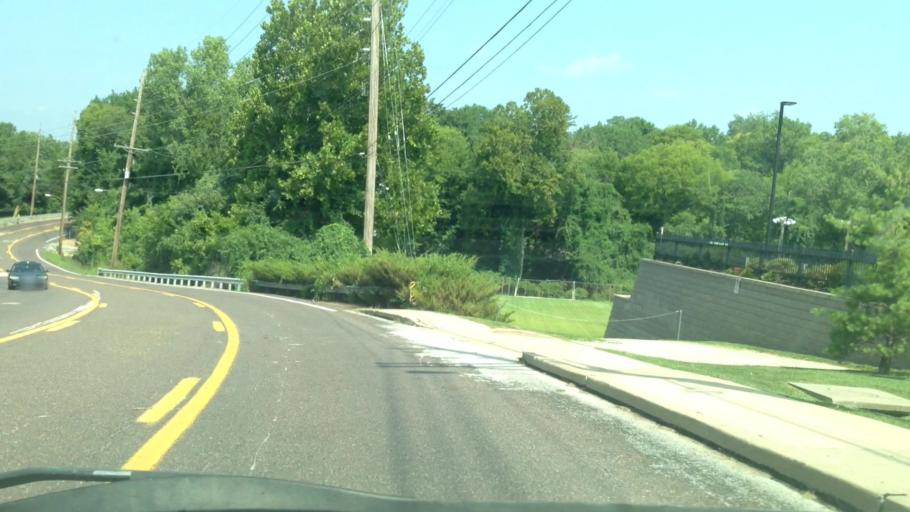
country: US
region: Missouri
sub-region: Saint Louis County
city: Des Peres
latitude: 38.5853
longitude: -90.4437
